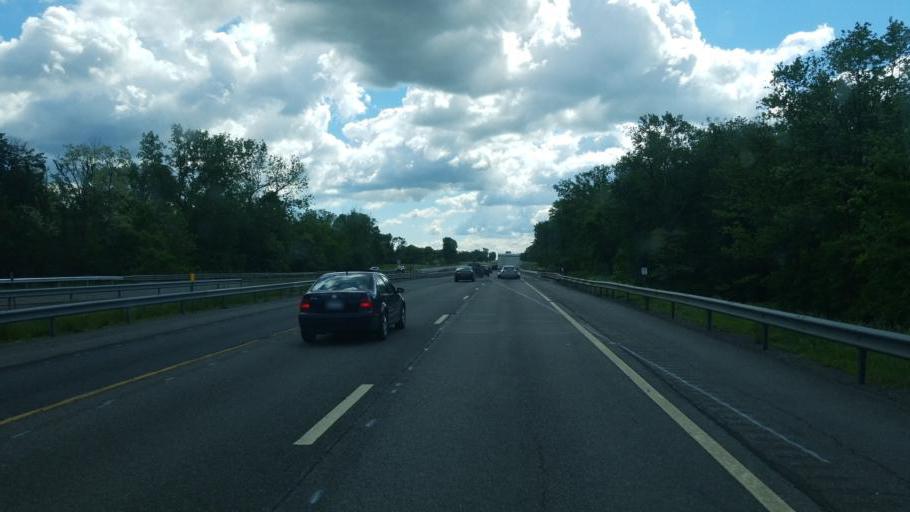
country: US
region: New York
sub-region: Onondaga County
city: Minoa
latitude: 43.0933
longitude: -75.9770
